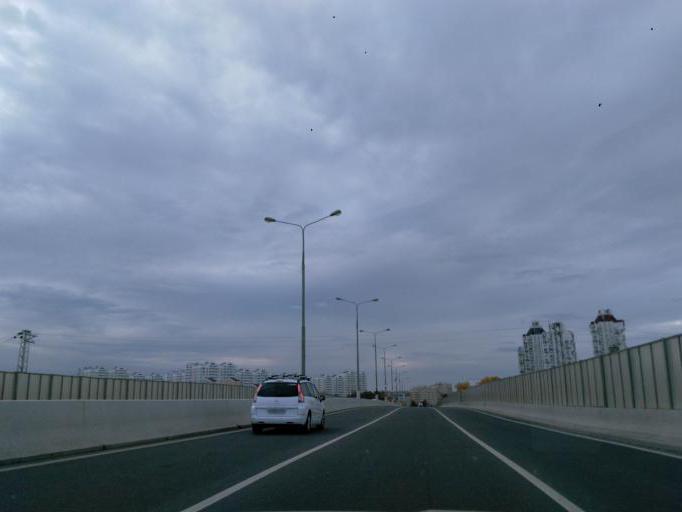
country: RU
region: Moscow
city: Zelenograd
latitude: 55.9808
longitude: 37.1738
